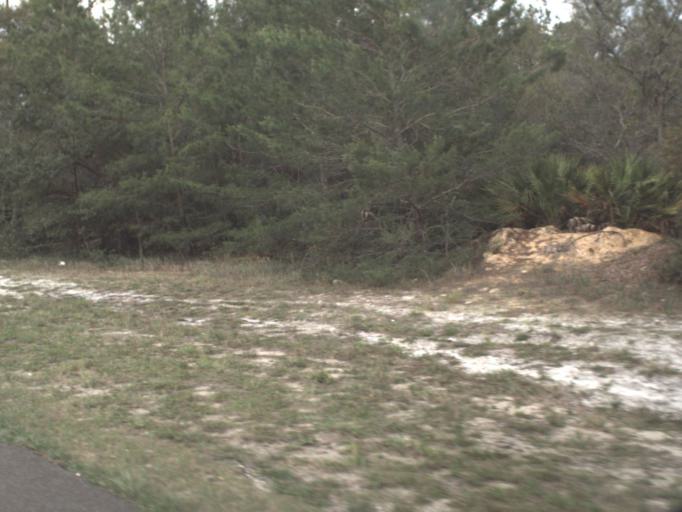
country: US
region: Florida
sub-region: Lake County
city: Umatilla
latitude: 29.0378
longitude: -81.6402
